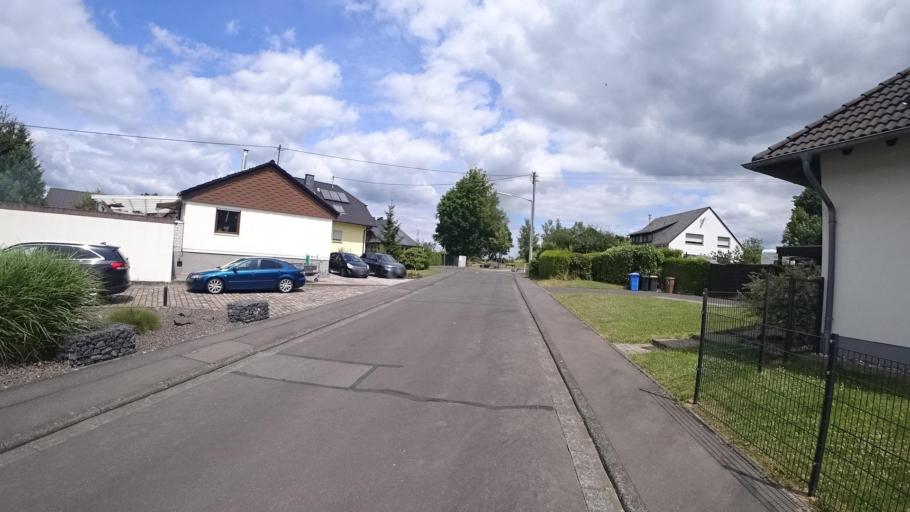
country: DE
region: Rheinland-Pfalz
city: Weyerbusch
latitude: 50.7158
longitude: 7.5566
